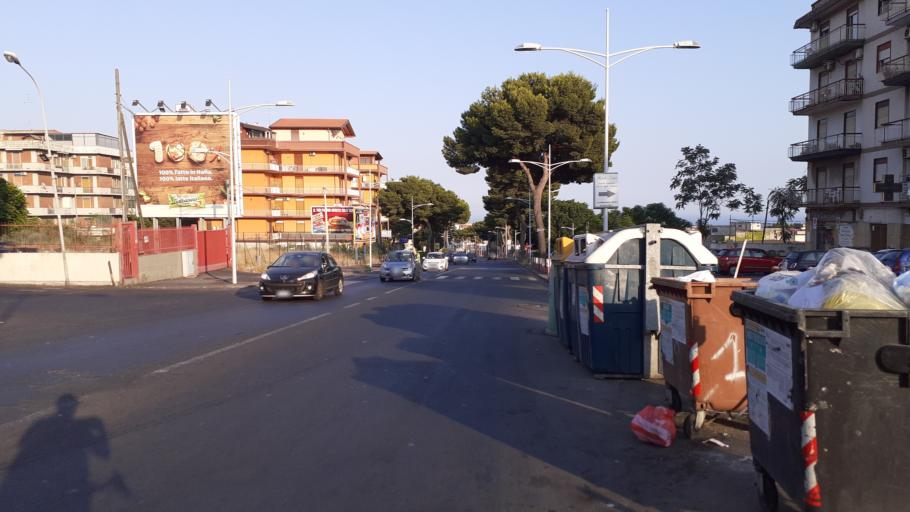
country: IT
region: Sicily
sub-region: Catania
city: Catania
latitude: 37.5064
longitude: 15.0523
